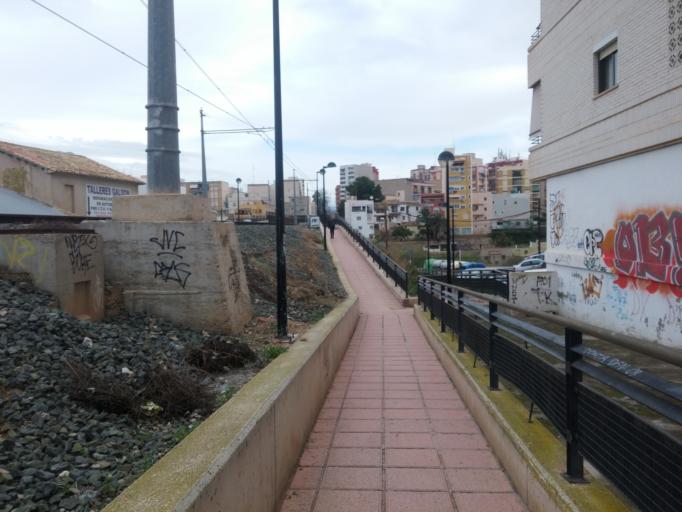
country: ES
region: Valencia
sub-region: Provincia de Alicante
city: Villajoyosa
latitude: 38.5063
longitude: -0.2359
